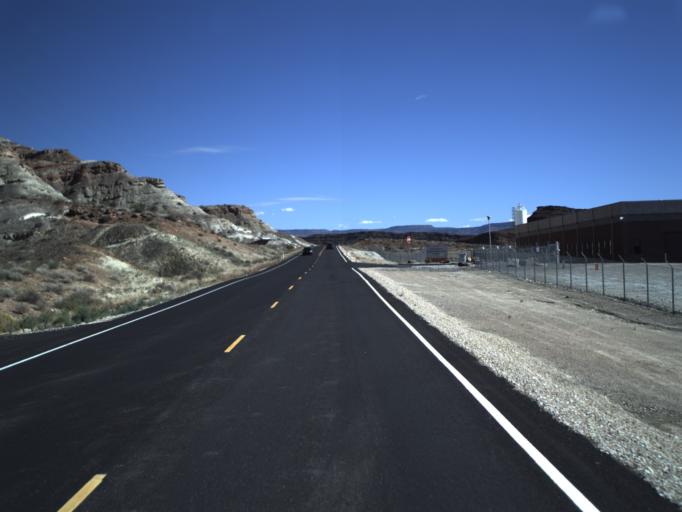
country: US
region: Utah
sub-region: Washington County
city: Hurricane
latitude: 37.1733
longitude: -113.4019
